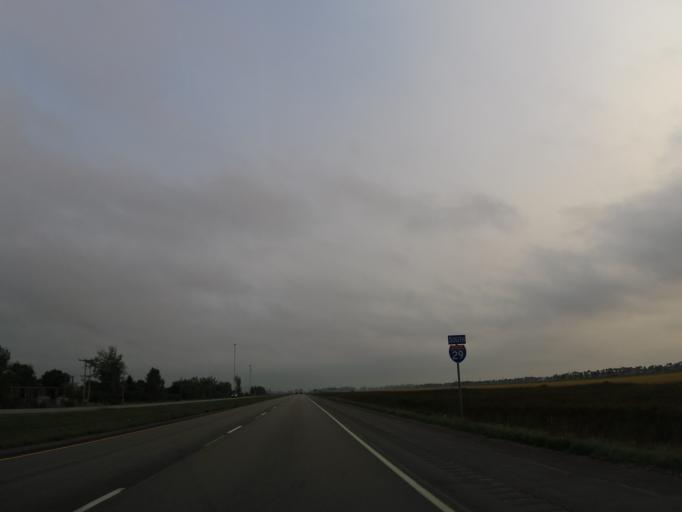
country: US
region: North Dakota
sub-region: Walsh County
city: Grafton
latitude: 48.5652
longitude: -97.1867
